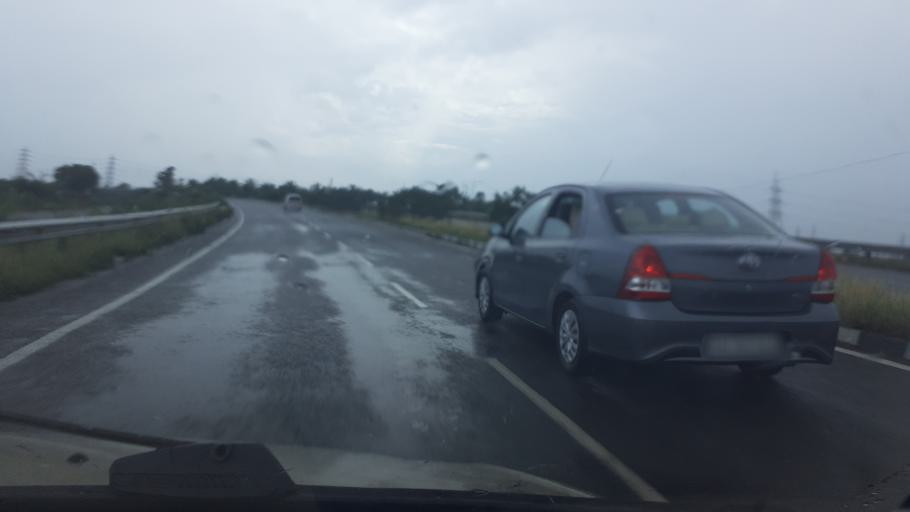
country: IN
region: Tamil Nadu
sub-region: Thoothukkudi
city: Kayattar
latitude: 8.9423
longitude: 77.7658
